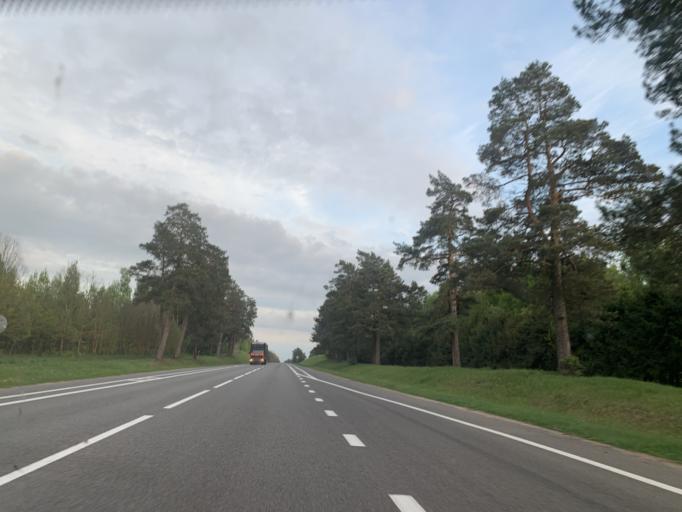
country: BY
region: Minsk
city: Haradzyeya
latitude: 53.2697
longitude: 26.6013
